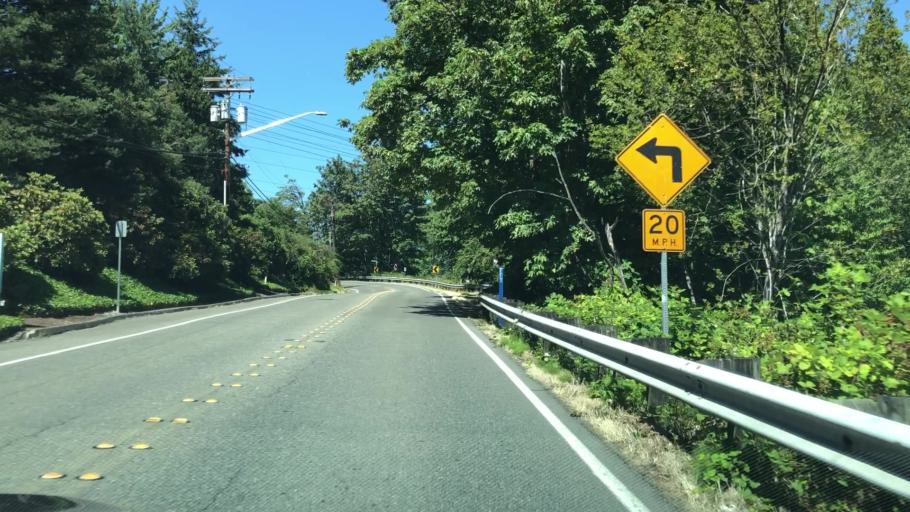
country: US
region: Washington
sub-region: King County
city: Woodinville
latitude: 47.7539
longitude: -122.1730
